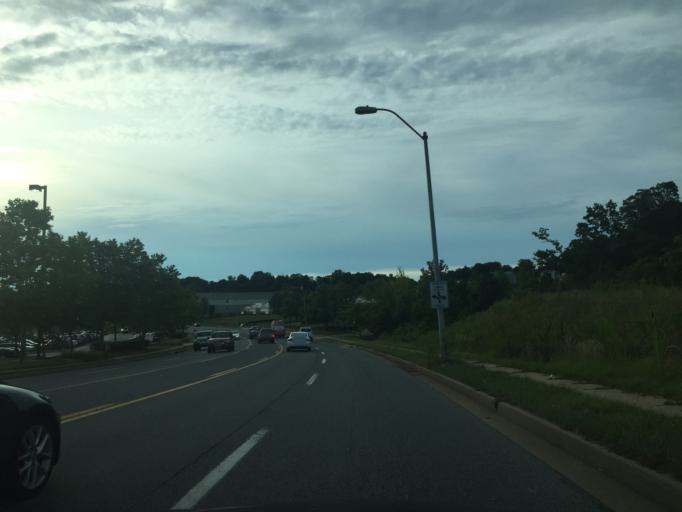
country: US
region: Maryland
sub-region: Baltimore County
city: Overlea
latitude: 39.3710
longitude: -76.5045
